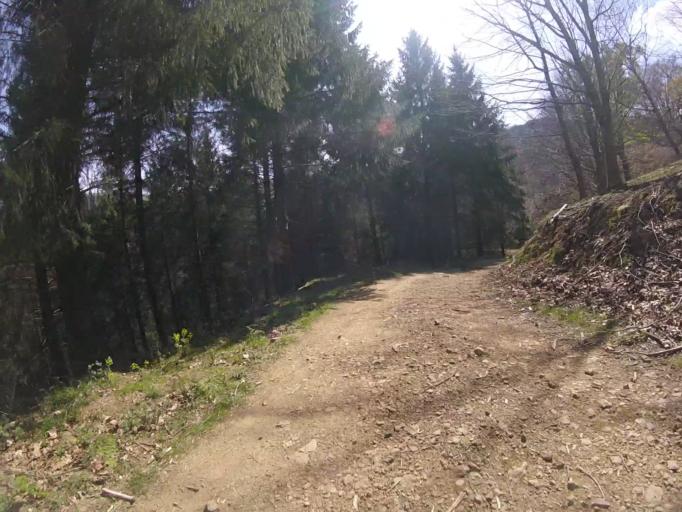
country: ES
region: Basque Country
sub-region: Provincia de Guipuzcoa
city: Irun
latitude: 43.2537
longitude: -1.8109
